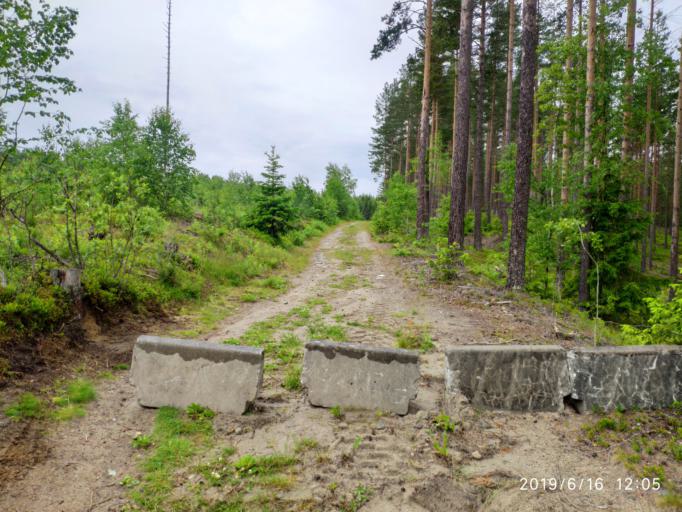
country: NO
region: Oppland
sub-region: Jevnaker
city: Jevnaker
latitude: 60.2217
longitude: 10.3452
